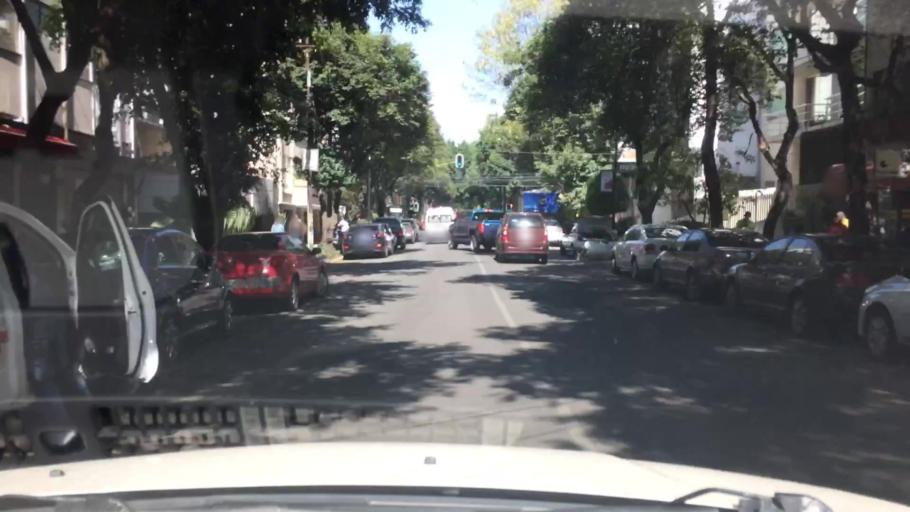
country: MX
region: Mexico City
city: Cuauhtemoc
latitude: 19.4302
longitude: -99.1654
